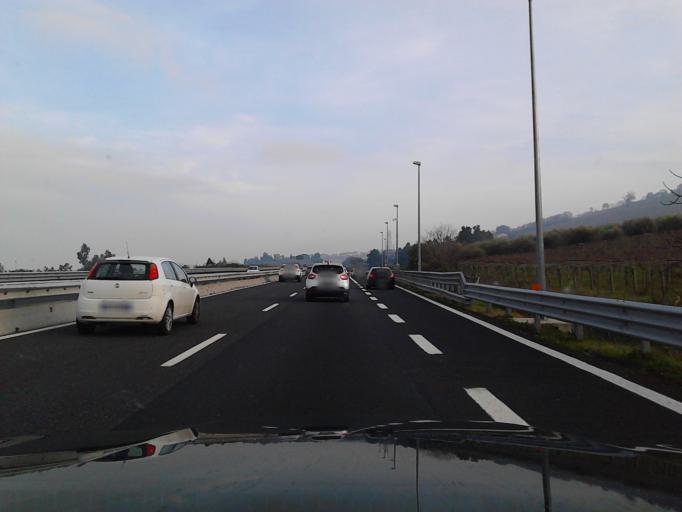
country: IT
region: Abruzzo
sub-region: Provincia di Teramo
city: Borgo Santa Maria Immacolata
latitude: 42.6073
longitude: 14.0443
